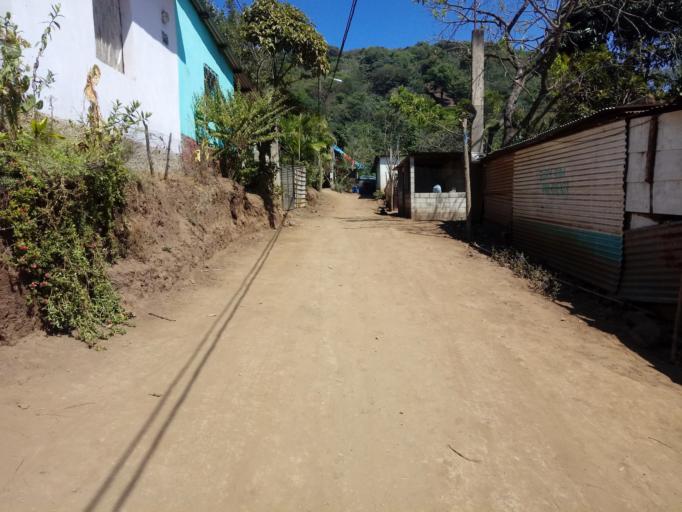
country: GT
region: Escuintla
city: San Vicente Pacaya
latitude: 14.4415
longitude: -90.6178
